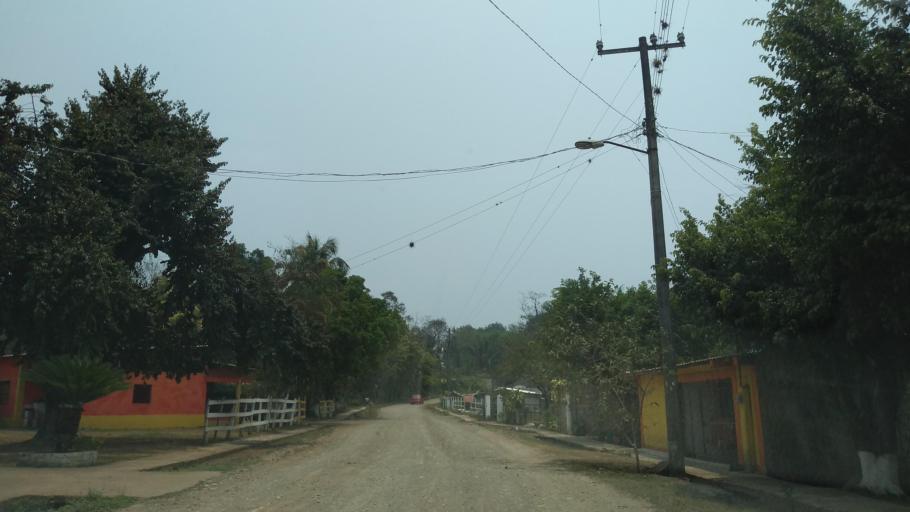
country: MX
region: Puebla
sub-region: San Sebastian Tlacotepec
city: San Martin Mazateopan
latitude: 18.4945
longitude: -96.7772
